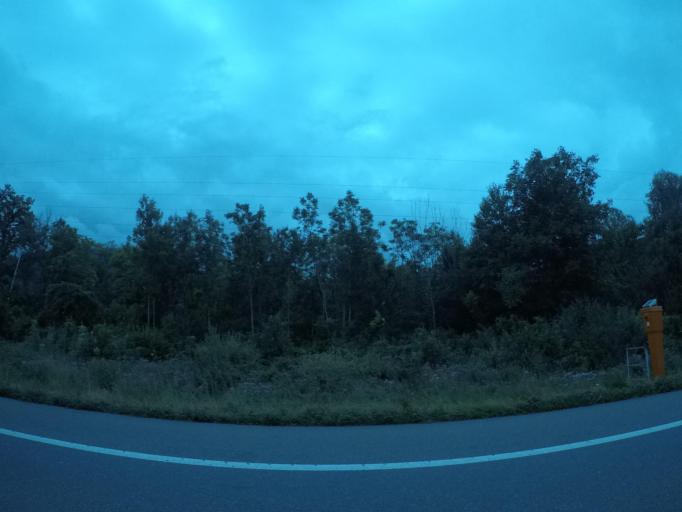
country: CH
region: Vaud
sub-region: Aigle District
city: Bex
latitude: 46.2549
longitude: 6.9863
